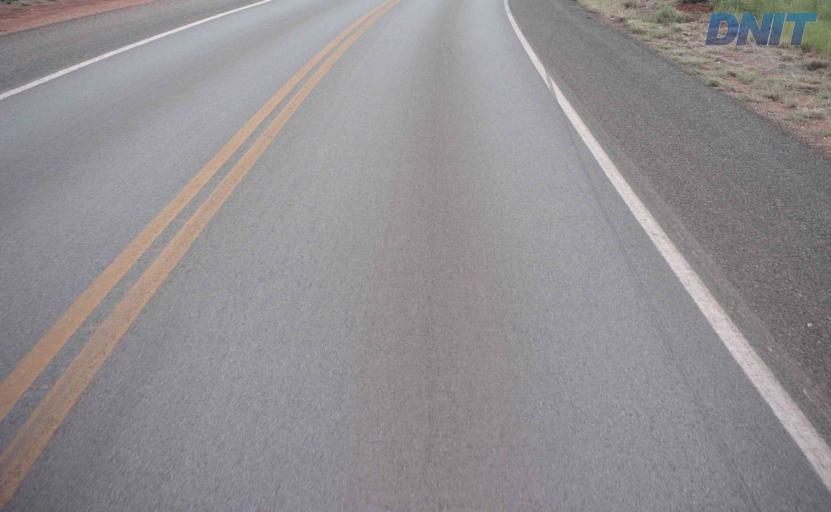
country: BR
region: Goias
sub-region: Barro Alto
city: Barro Alto
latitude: -15.2094
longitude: -48.6718
